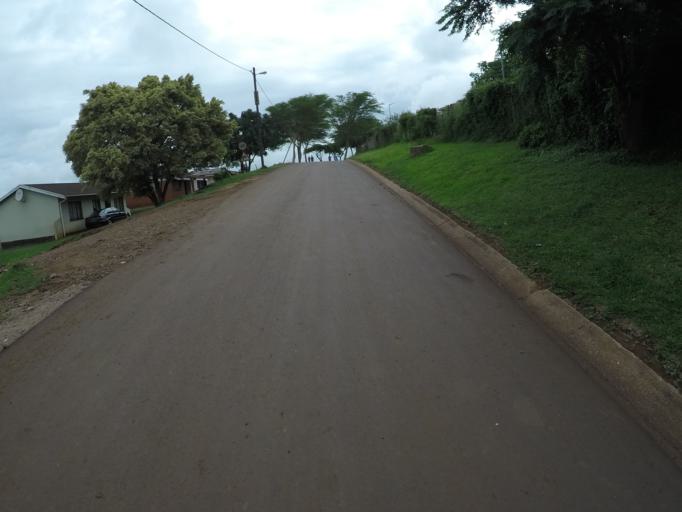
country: ZA
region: KwaZulu-Natal
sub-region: uThungulu District Municipality
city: Empangeni
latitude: -28.7802
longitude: 31.8666
